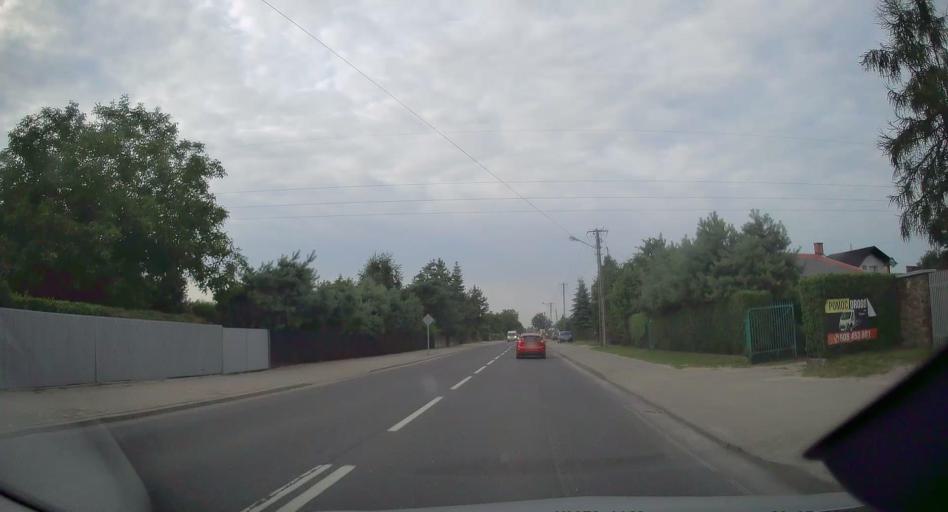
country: PL
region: Lodz Voivodeship
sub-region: Powiat radomszczanski
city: Radomsko
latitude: 51.0887
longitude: 19.4555
